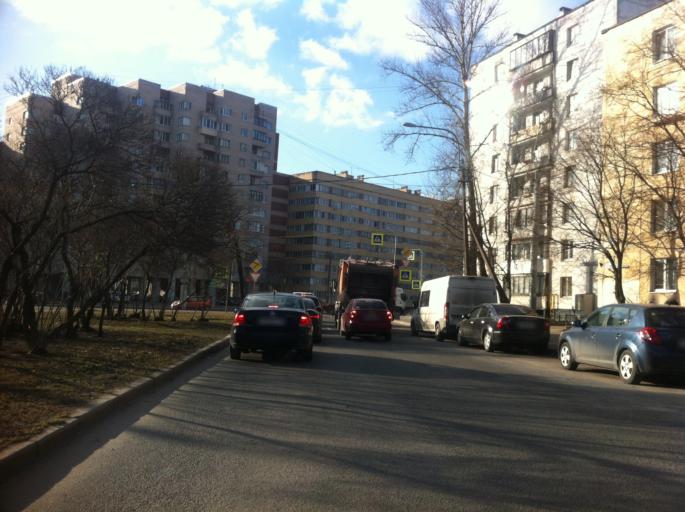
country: RU
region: St.-Petersburg
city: Dachnoye
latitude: 59.8474
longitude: 30.2571
